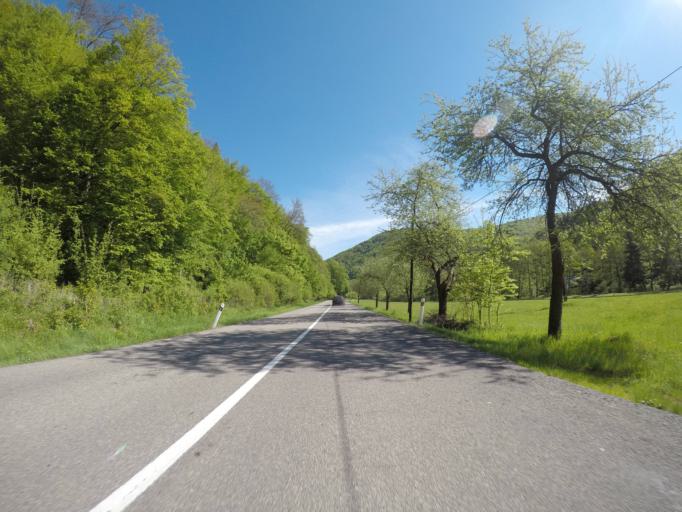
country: SK
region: Banskobystricky
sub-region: Okres Banska Bystrica
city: Banska Stiavnica
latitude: 48.5164
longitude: 19.0024
